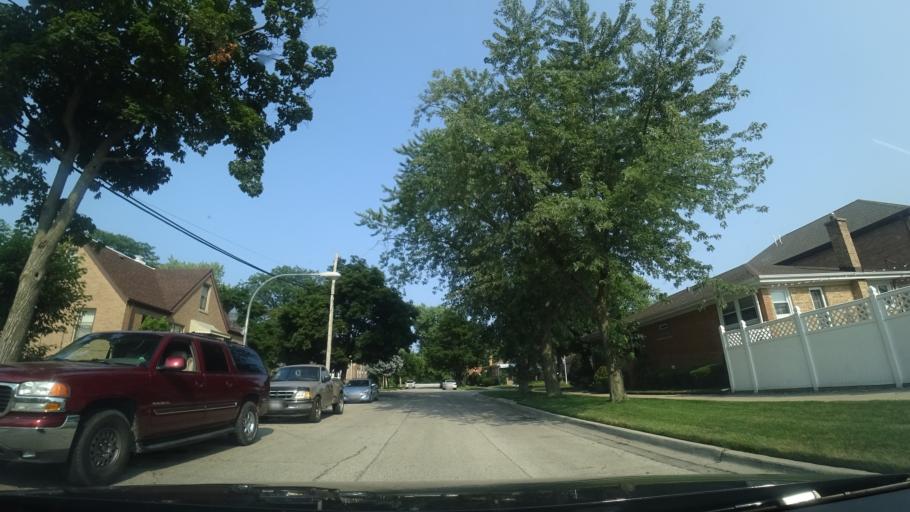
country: US
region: Illinois
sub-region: Cook County
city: Lincolnwood
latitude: 41.9937
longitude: -87.7306
